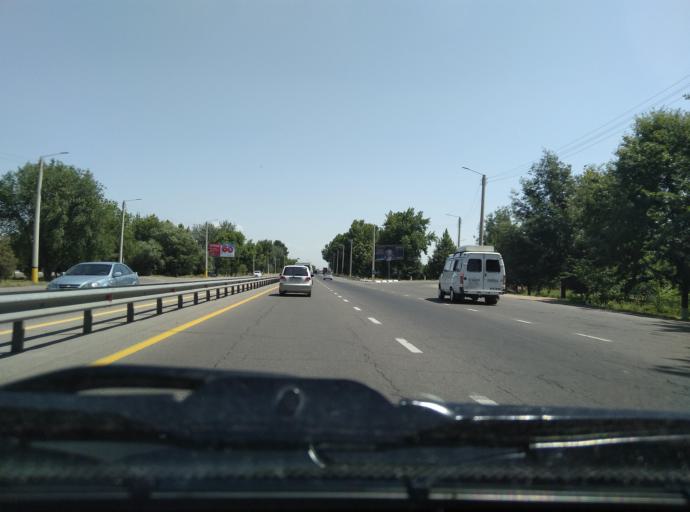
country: UZ
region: Toshkent Shahri
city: Bektemir
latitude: 41.2443
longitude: 69.3965
